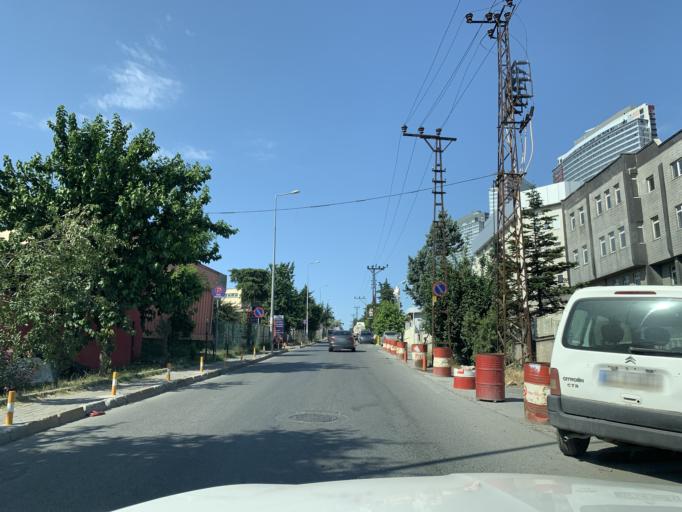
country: TR
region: Istanbul
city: Esenyurt
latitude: 41.0591
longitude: 28.6612
